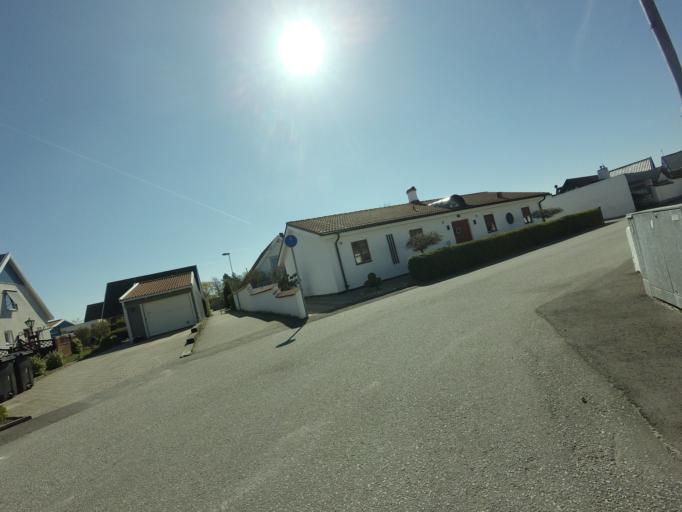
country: SE
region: Skane
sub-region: Trelleborgs Kommun
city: Trelleborg
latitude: 55.3780
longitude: 13.1172
